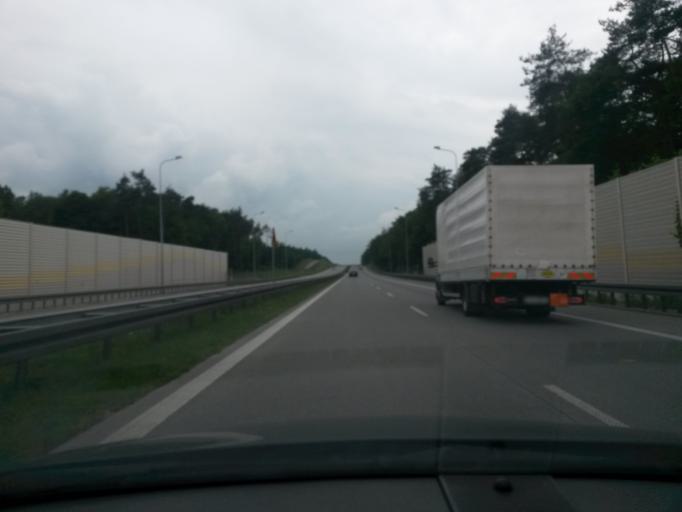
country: PL
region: Lodz Voivodeship
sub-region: Powiat skierniewicki
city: Kowiesy
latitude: 51.8374
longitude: 20.3445
